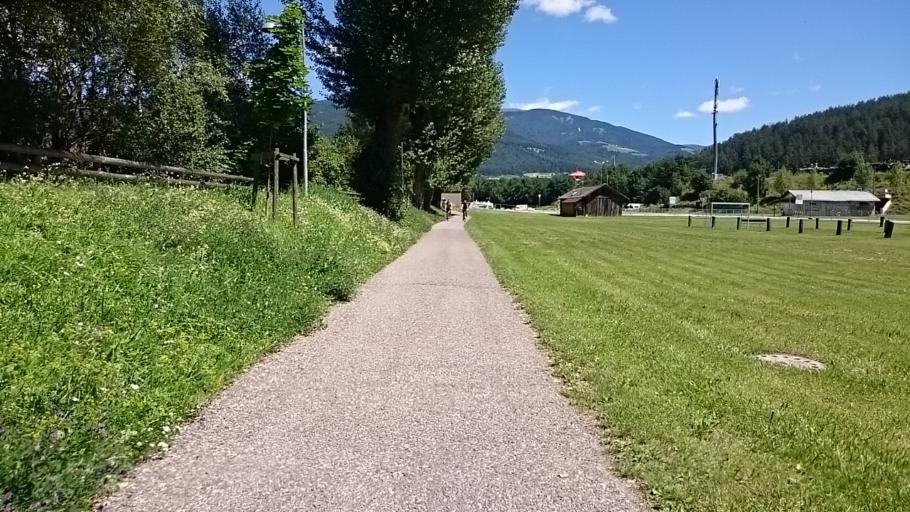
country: IT
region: Trentino-Alto Adige
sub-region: Bolzano
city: Brunico
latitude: 46.7941
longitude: 11.9247
